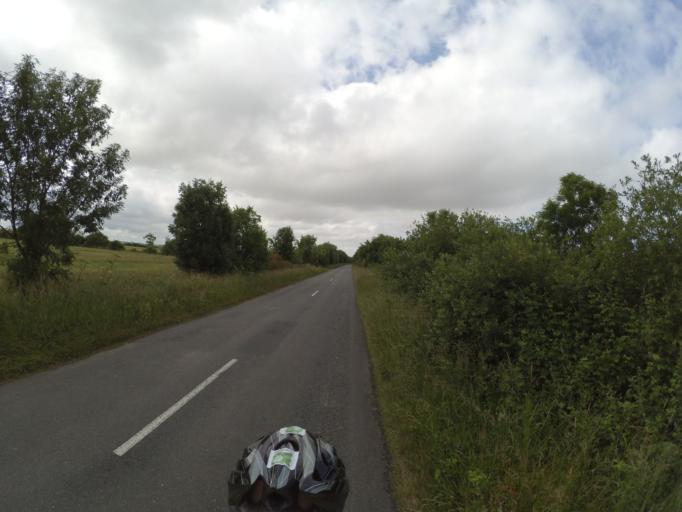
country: FR
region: Poitou-Charentes
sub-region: Departement de la Charente-Maritime
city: Yves
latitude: 46.0403
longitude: -1.0420
